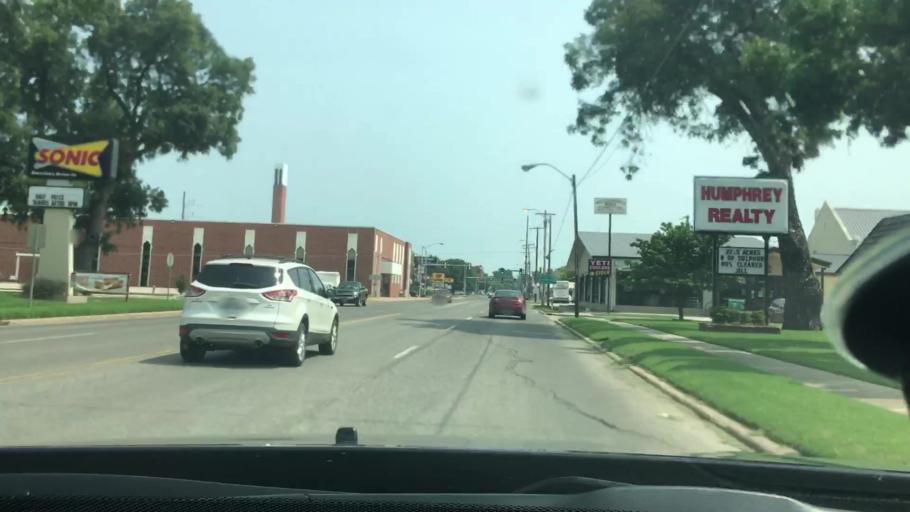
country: US
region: Oklahoma
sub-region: Garvin County
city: Pauls Valley
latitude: 34.7381
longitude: -97.2245
